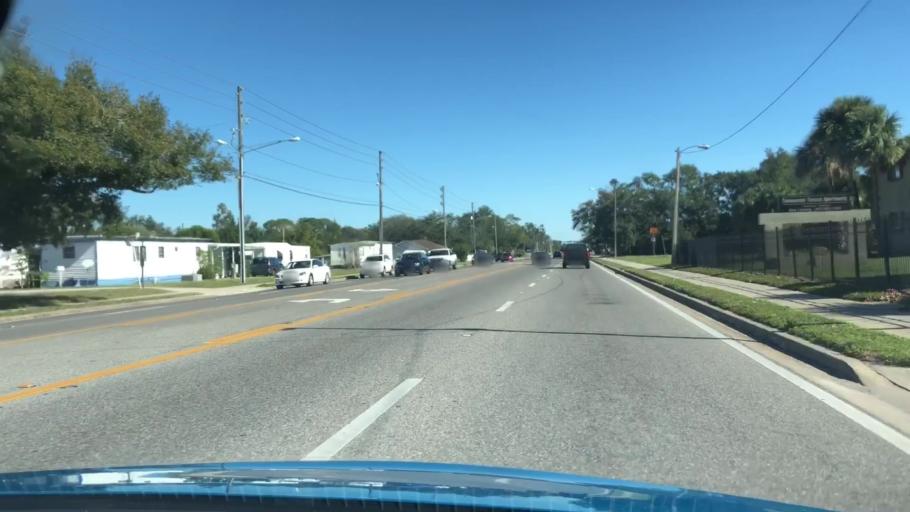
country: US
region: Florida
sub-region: Orange County
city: Sky Lake
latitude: 28.4726
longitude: -81.3919
